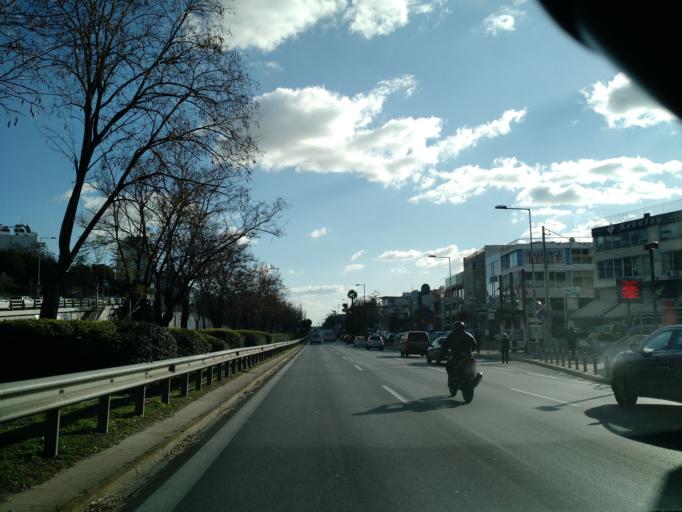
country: GR
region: Attica
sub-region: Nomarchia Athinas
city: Agios Dimitrios
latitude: 37.9297
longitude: 23.7444
